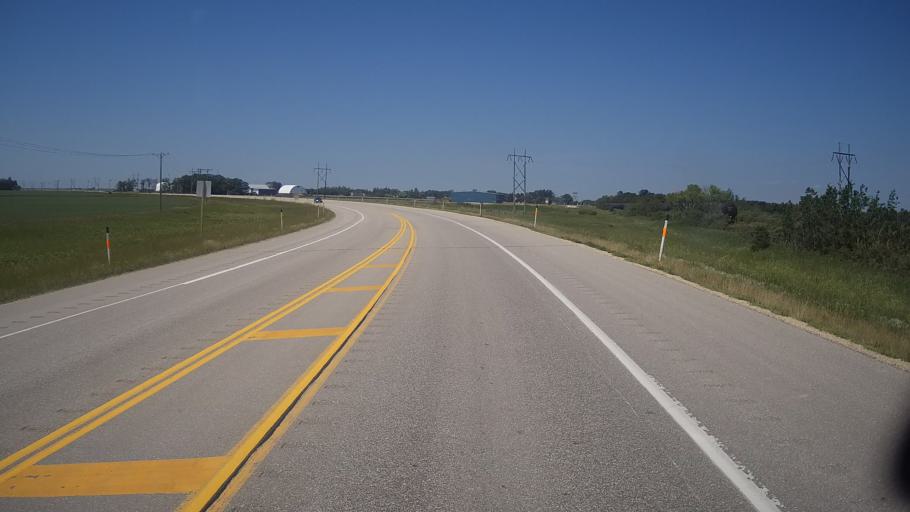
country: CA
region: Manitoba
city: Stonewall
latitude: 50.1217
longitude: -97.5308
